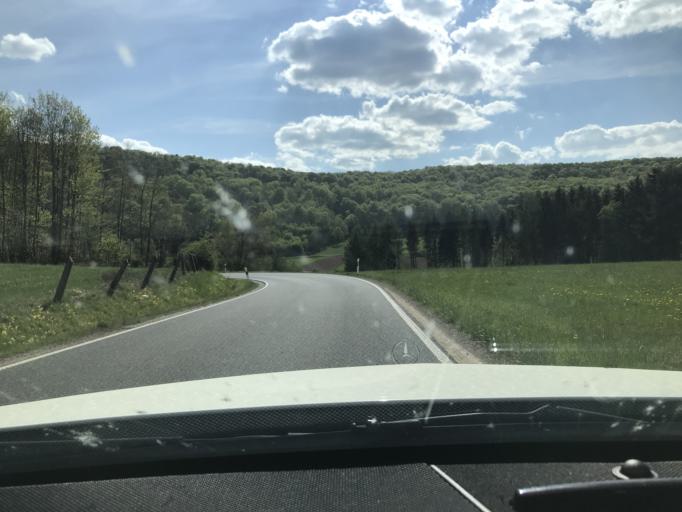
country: DE
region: Hesse
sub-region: Regierungsbezirk Kassel
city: Weissenborn
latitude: 51.1181
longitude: 10.0942
